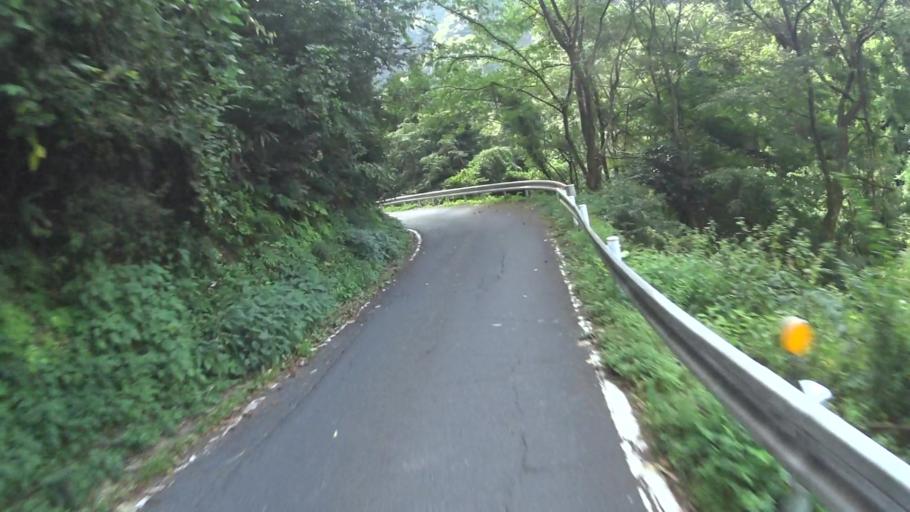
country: JP
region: Kyoto
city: Miyazu
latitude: 35.6357
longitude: 135.1951
